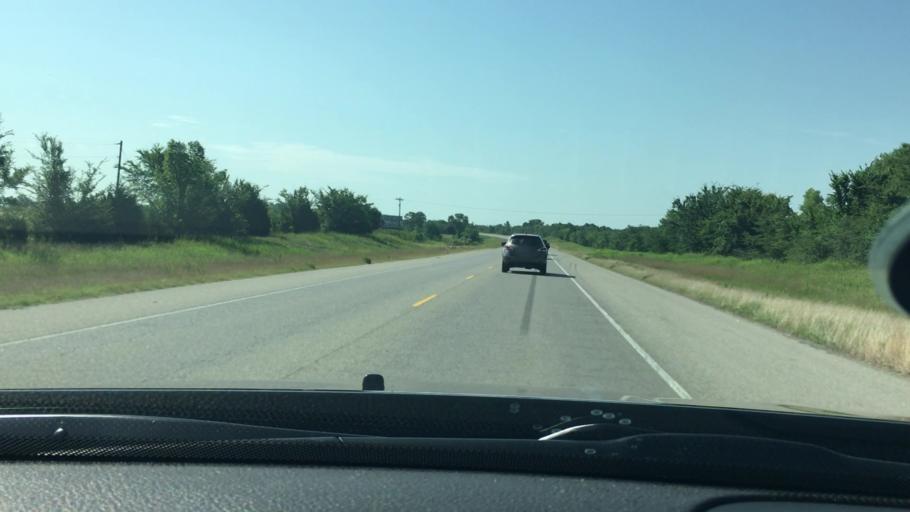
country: US
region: Oklahoma
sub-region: Pontotoc County
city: Ada
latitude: 34.6524
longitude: -96.5551
